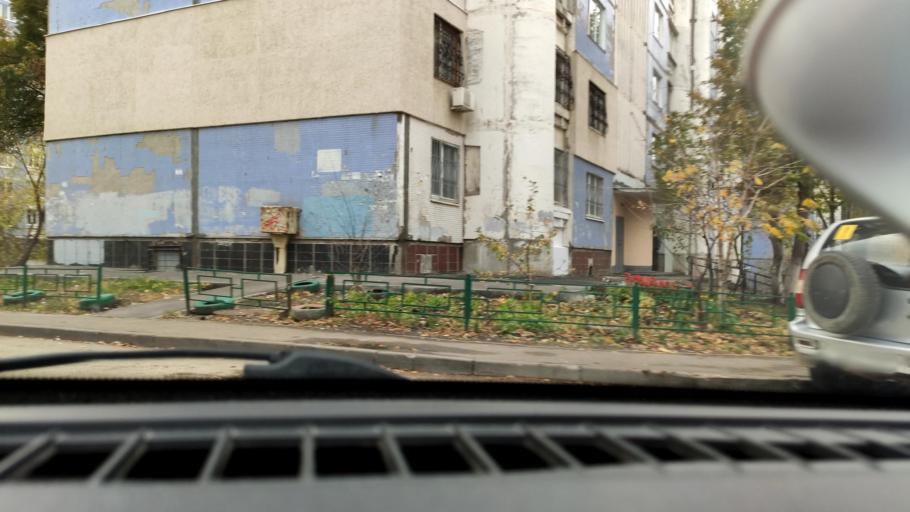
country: RU
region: Samara
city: Samara
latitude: 53.2409
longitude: 50.1921
